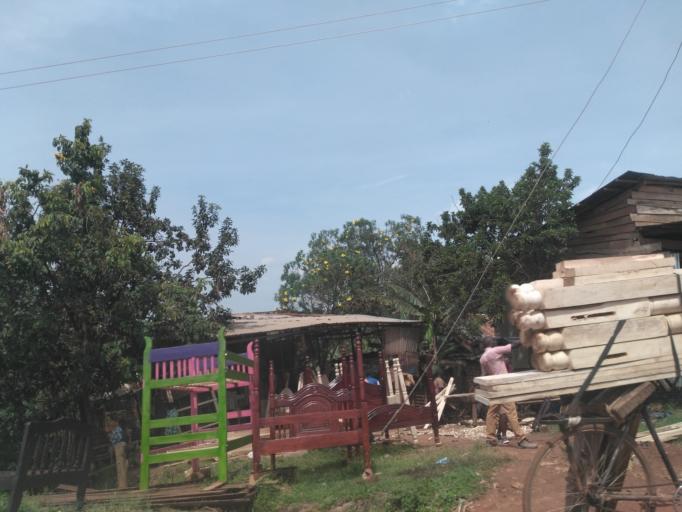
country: UG
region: Central Region
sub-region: Wakiso District
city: Kireka
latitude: 0.4462
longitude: 32.6117
